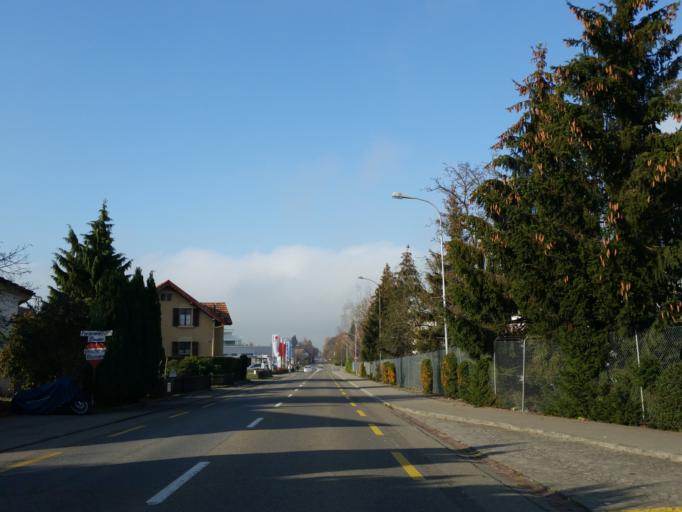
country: CH
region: Thurgau
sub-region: Arbon District
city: Arbon
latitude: 47.5220
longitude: 9.4127
